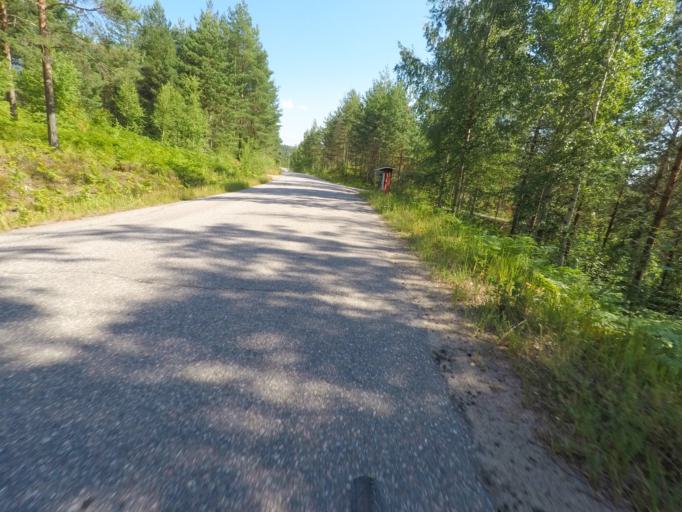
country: FI
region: Southern Savonia
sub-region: Mikkeli
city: Puumala
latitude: 61.4215
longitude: 28.1069
